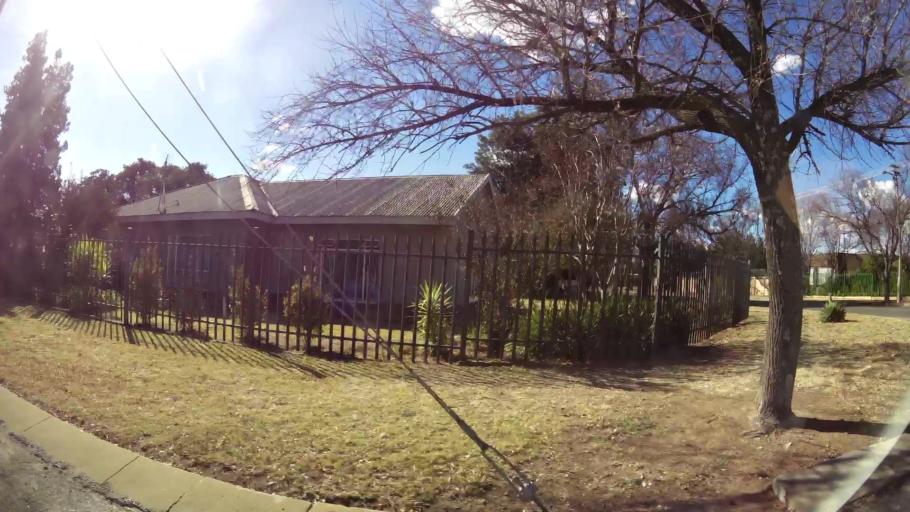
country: ZA
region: North-West
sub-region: Dr Kenneth Kaunda District Municipality
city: Klerksdorp
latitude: -26.8590
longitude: 26.6400
